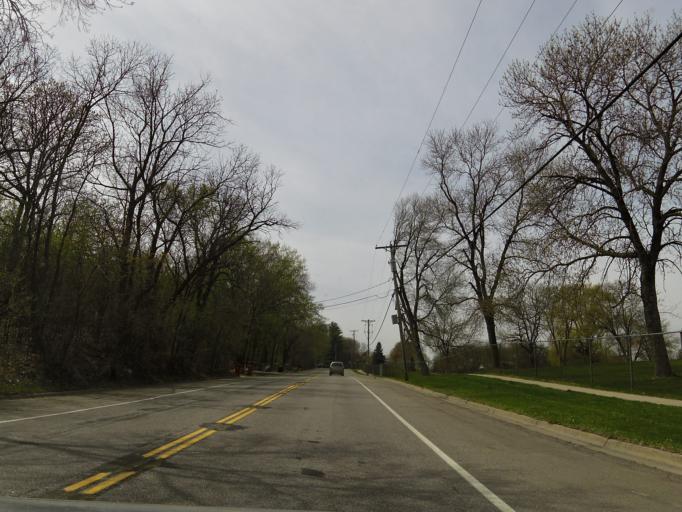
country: US
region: Minnesota
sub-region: Scott County
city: Savage
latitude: 44.8188
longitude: -93.3558
